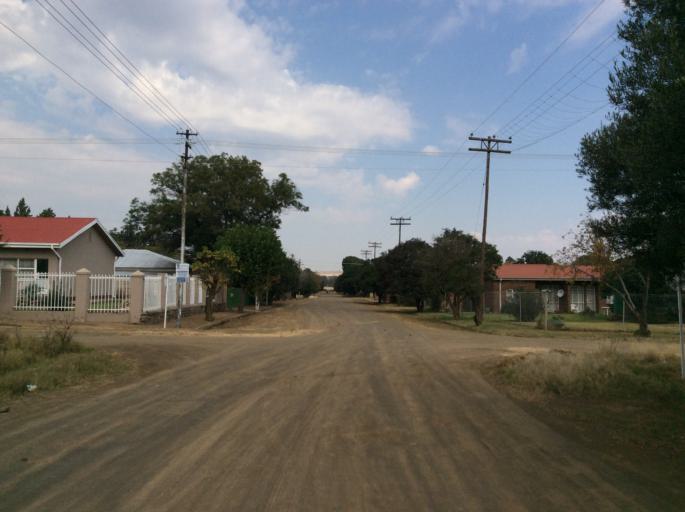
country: LS
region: Mafeteng
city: Mafeteng
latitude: -29.7283
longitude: 27.0409
